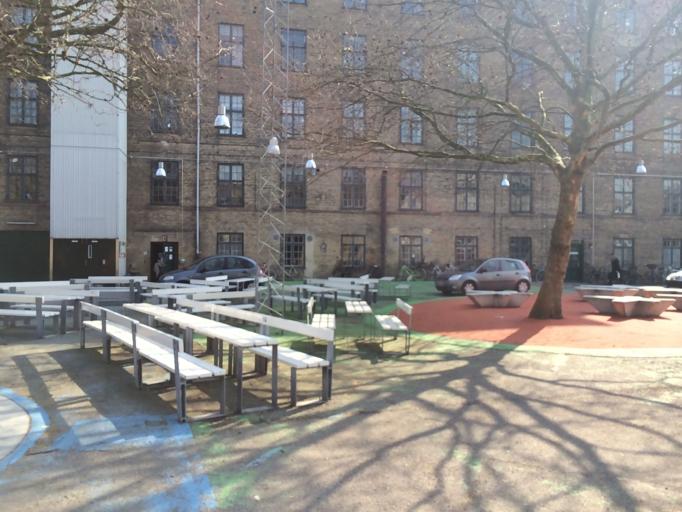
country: DK
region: Capital Region
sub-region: Frederiksberg Kommune
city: Frederiksberg
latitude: 55.6620
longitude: 12.5403
